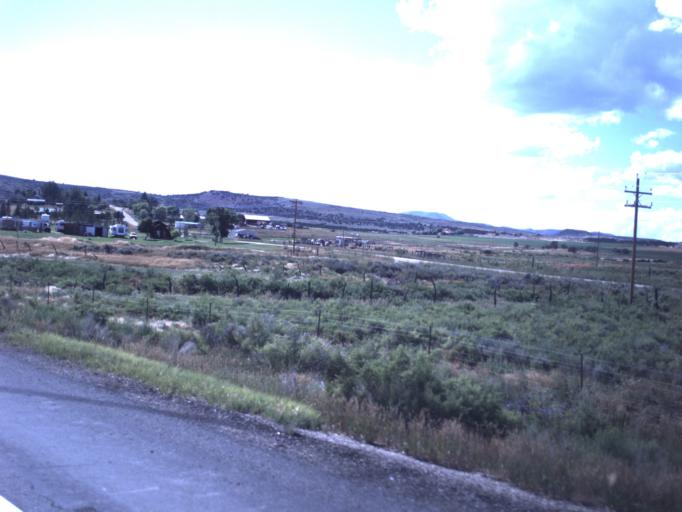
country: US
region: Utah
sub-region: Duchesne County
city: Duchesne
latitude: 40.2119
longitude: -110.8640
